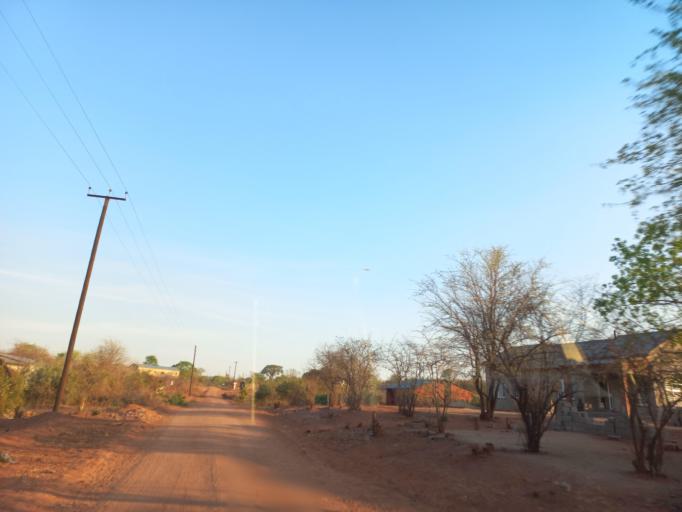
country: ZM
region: Lusaka
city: Luangwa
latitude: -15.6230
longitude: 30.3931
